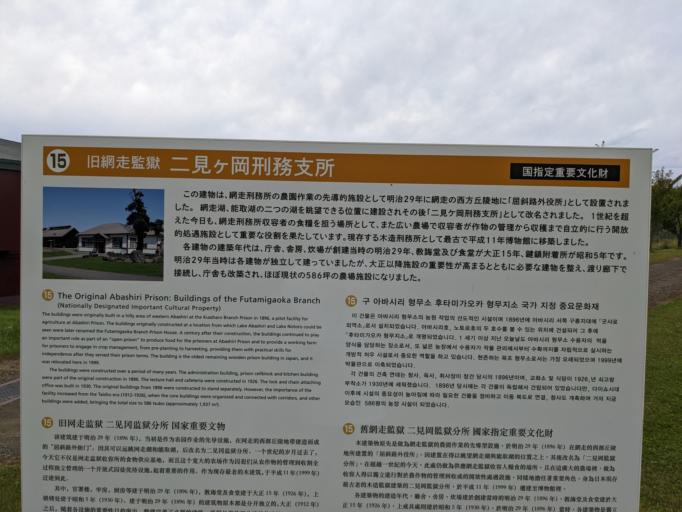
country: JP
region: Hokkaido
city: Abashiri
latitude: 43.9967
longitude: 144.2312
